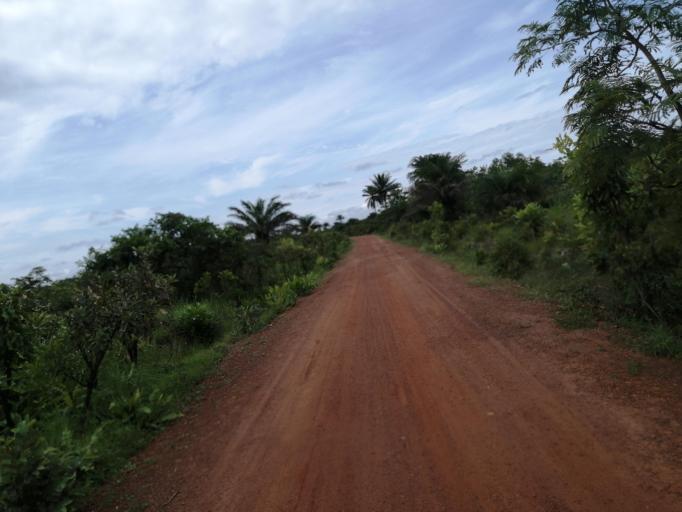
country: SL
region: Northern Province
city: Port Loko
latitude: 8.7717
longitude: -12.9145
